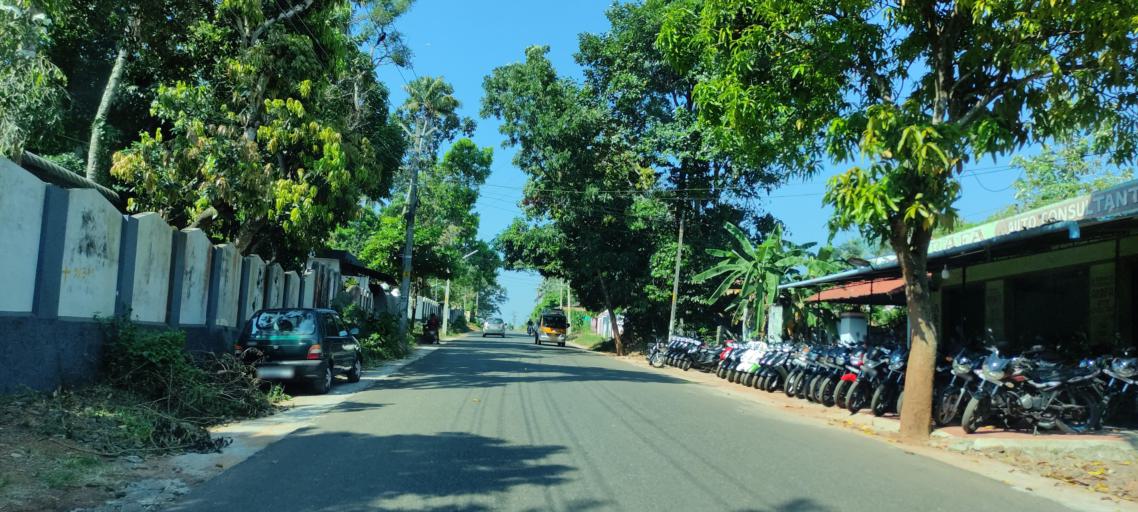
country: IN
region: Kerala
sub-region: Kollam
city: Panmana
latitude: 9.0421
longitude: 76.6110
